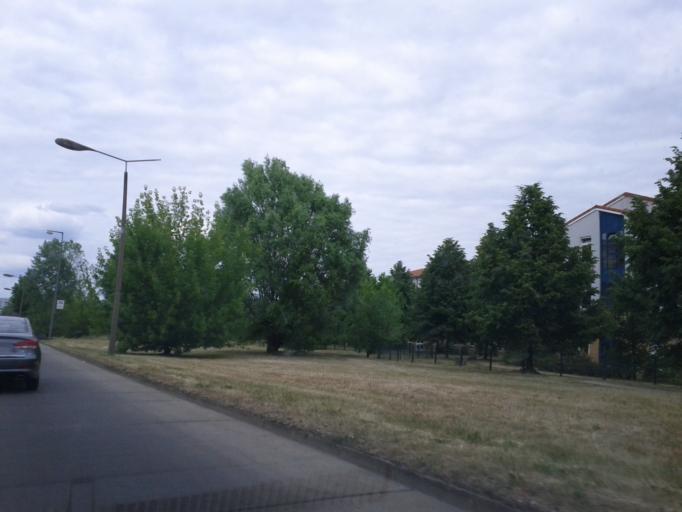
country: DE
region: Berlin
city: Marzahn
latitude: 52.5557
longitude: 13.5748
